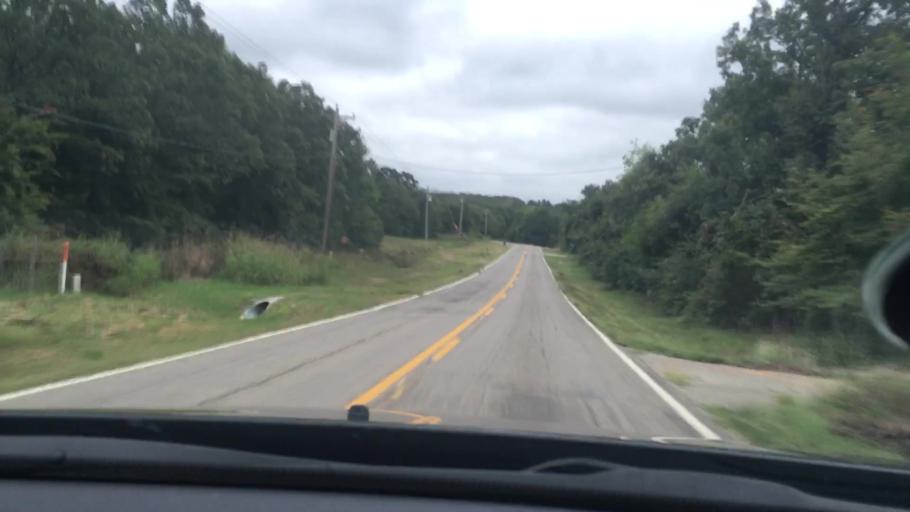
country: US
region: Oklahoma
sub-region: Sequoyah County
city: Vian
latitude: 35.6025
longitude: -95.0084
